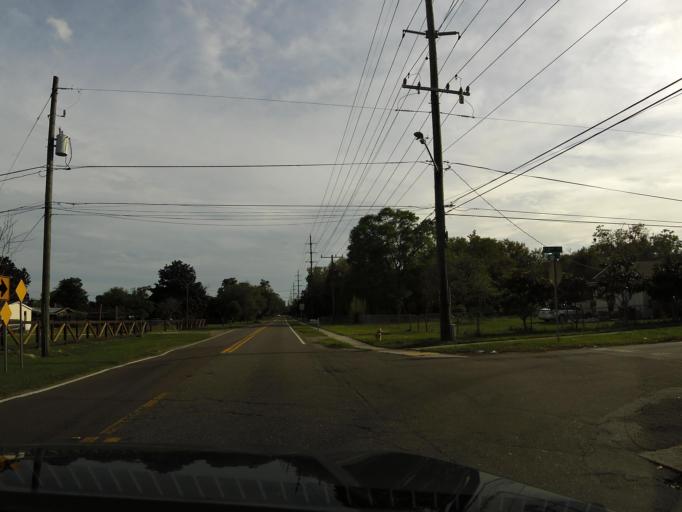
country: US
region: Florida
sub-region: Clay County
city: Bellair-Meadowbrook Terrace
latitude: 30.2336
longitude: -81.7644
